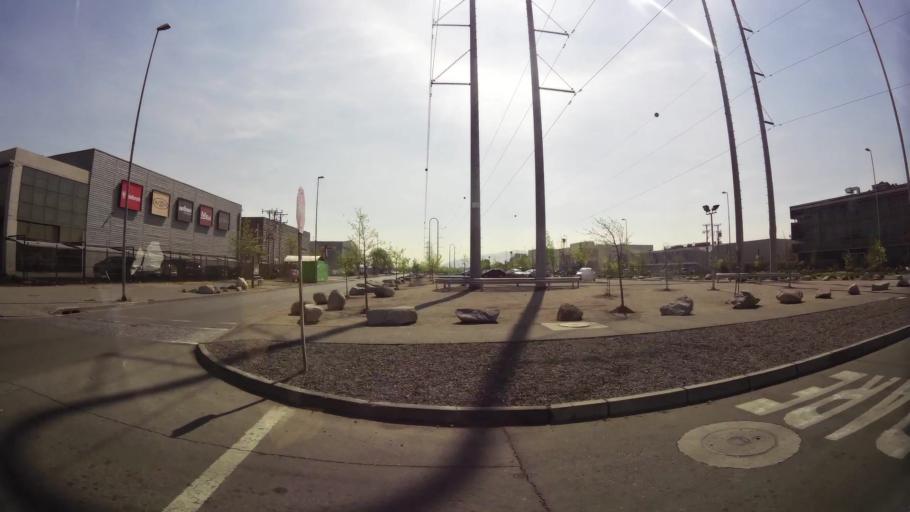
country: CL
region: Santiago Metropolitan
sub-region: Provincia de Santiago
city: Lo Prado
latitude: -33.4286
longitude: -70.7761
